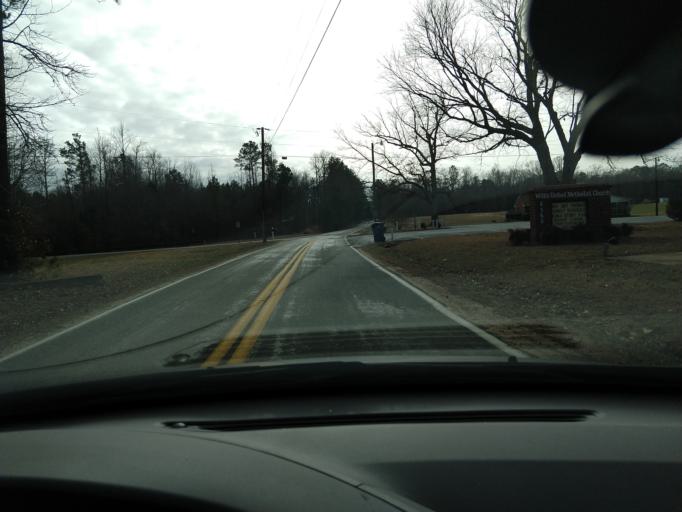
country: US
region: Virginia
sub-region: Henrico County
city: Fort Lee
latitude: 37.4349
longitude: -77.2356
